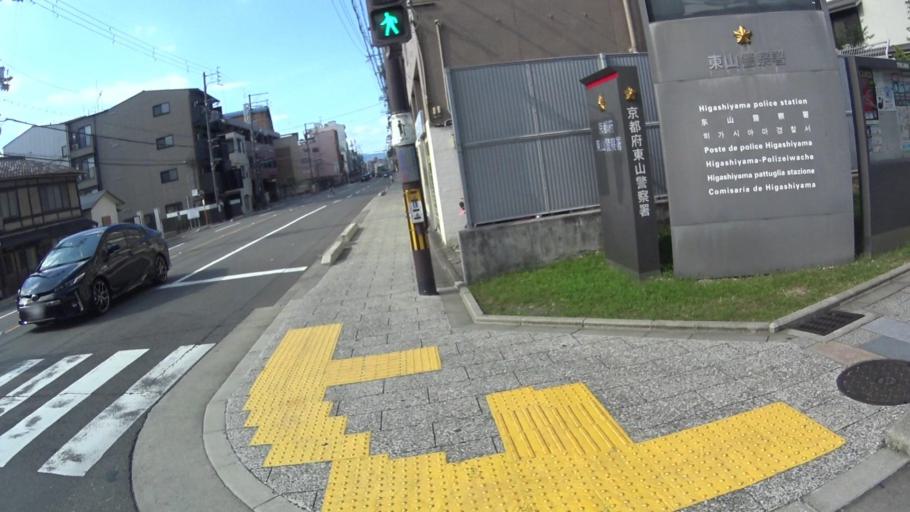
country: RU
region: Rostov
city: Remontnoye
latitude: 46.4989
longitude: 43.7790
